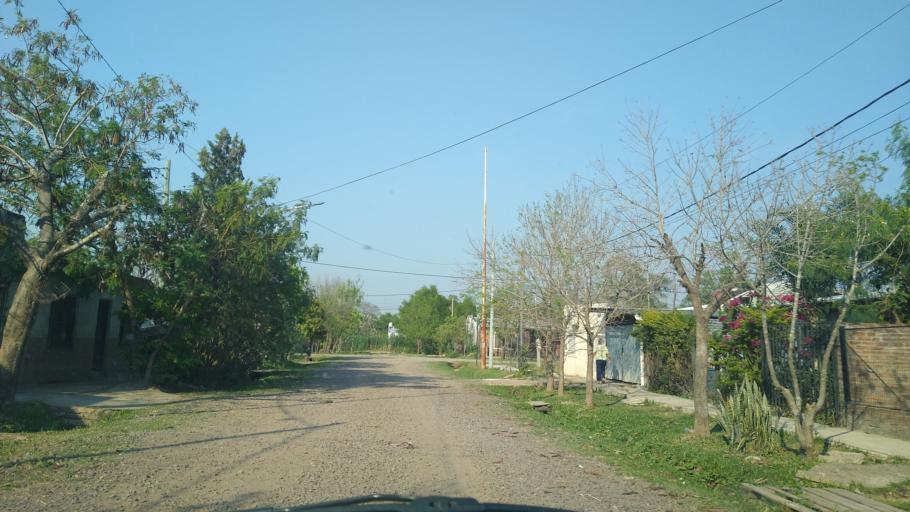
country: AR
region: Chaco
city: Barranqueras
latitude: -27.4763
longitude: -58.9504
